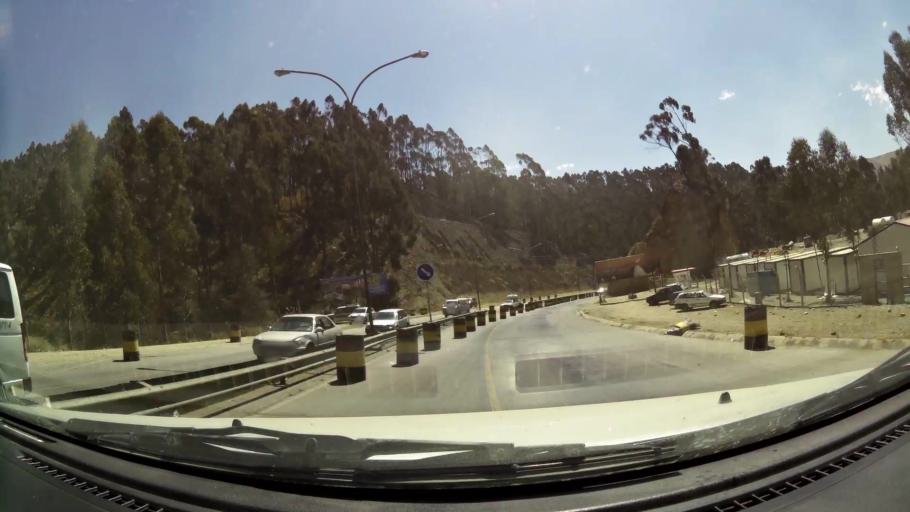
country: BO
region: La Paz
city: La Paz
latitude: -16.4730
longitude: -68.1601
